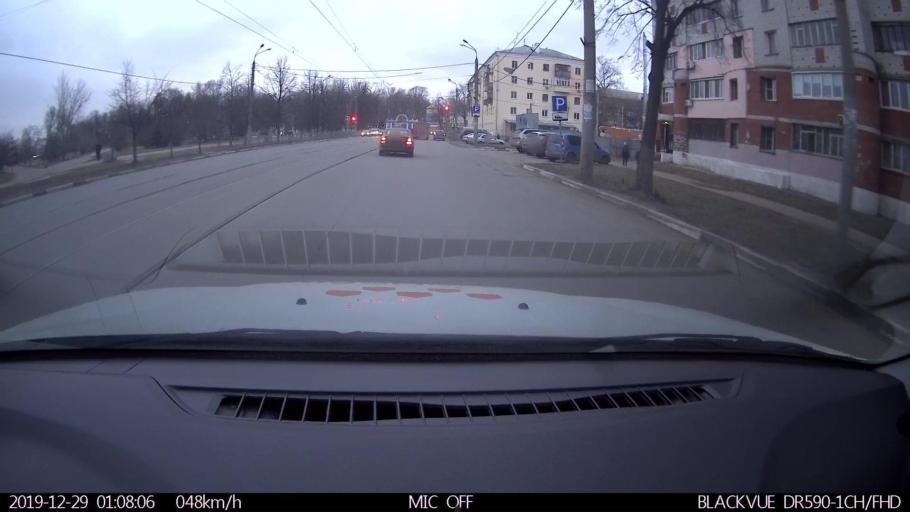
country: RU
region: Nizjnij Novgorod
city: Nizhniy Novgorod
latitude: 56.3142
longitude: 43.9380
